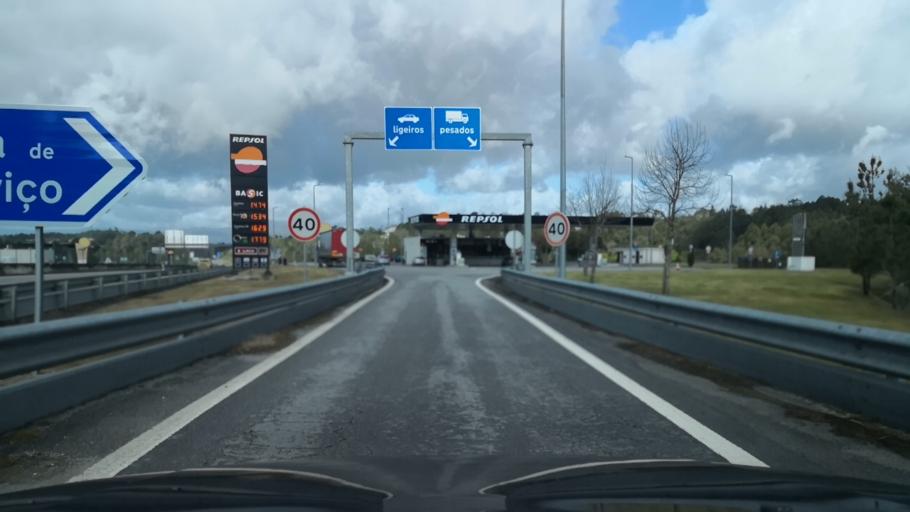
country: PT
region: Viseu
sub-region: Viseu
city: Viseu
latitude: 40.6241
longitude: -7.9304
